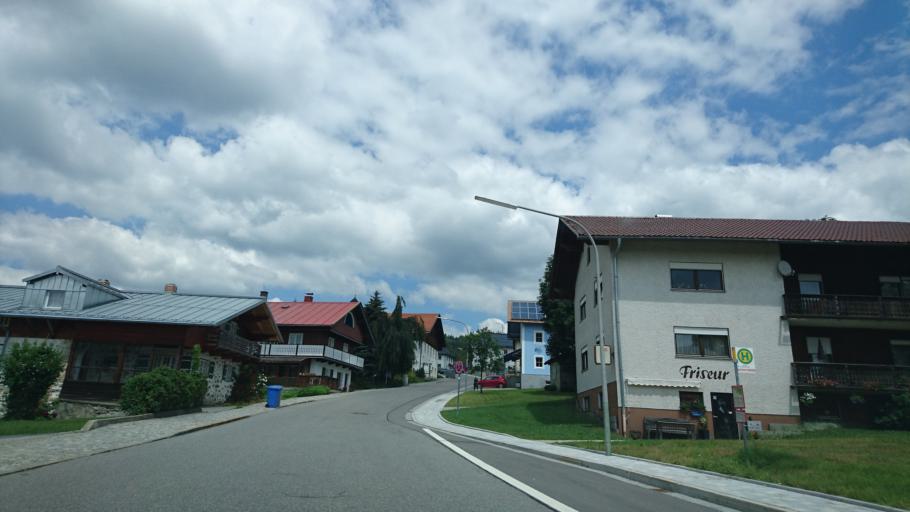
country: DE
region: Bavaria
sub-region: Lower Bavaria
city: Mauth
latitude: 48.8872
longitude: 13.5839
